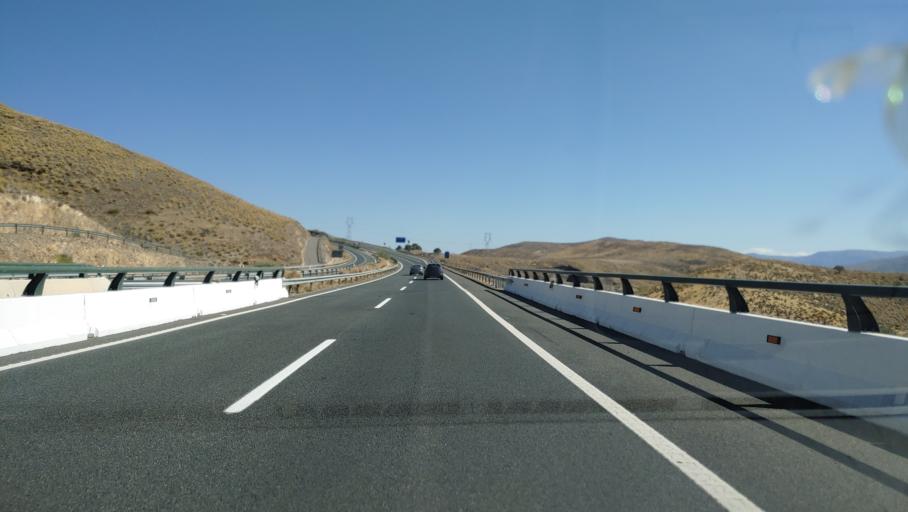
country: ES
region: Andalusia
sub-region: Provincia de Almeria
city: Gergal
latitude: 37.1319
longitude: -2.6409
